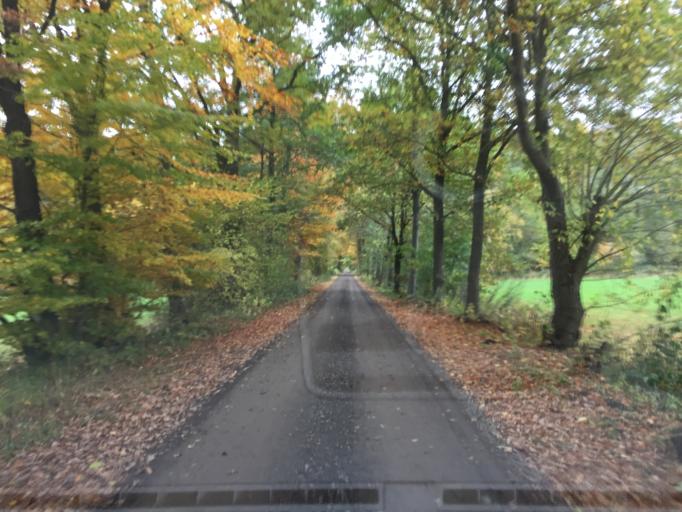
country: DE
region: Lower Saxony
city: Linsburg
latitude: 52.5812
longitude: 9.3141
